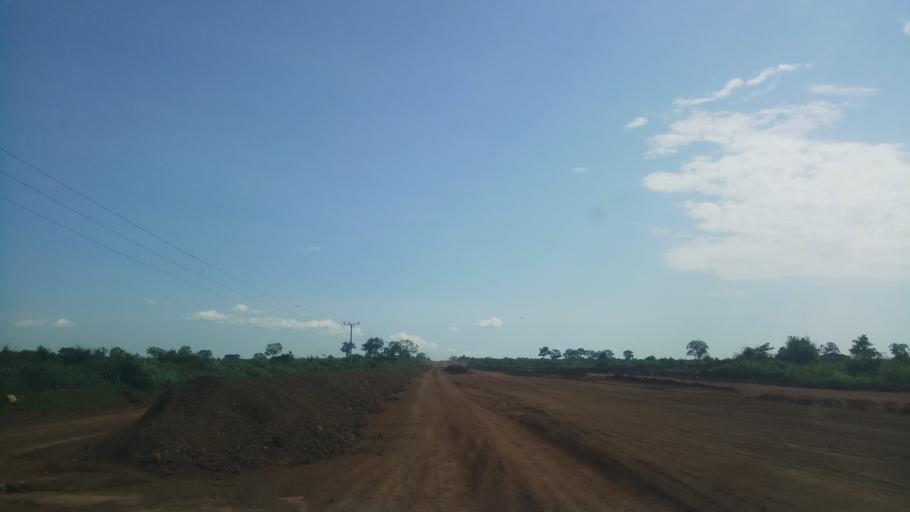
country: ET
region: Gambela
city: Gambela
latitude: 8.1842
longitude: 34.4971
